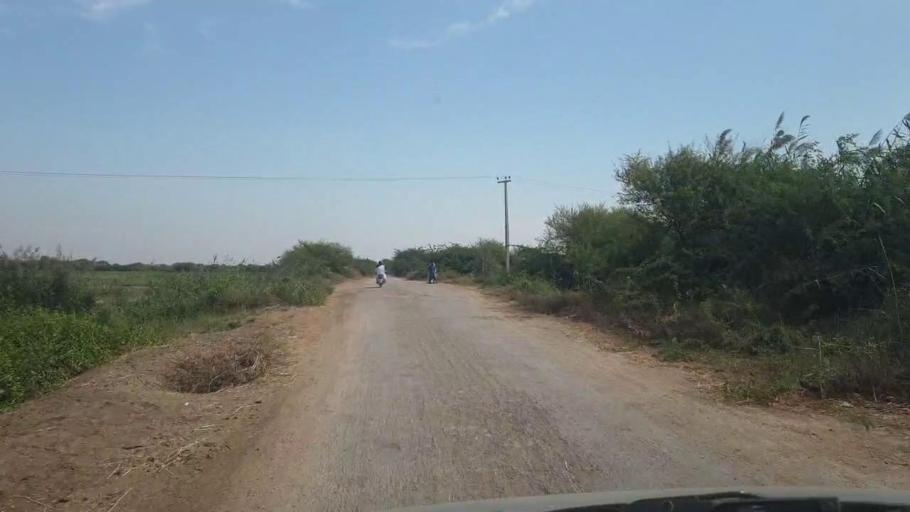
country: PK
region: Sindh
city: Tando Bago
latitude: 24.9096
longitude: 69.0316
